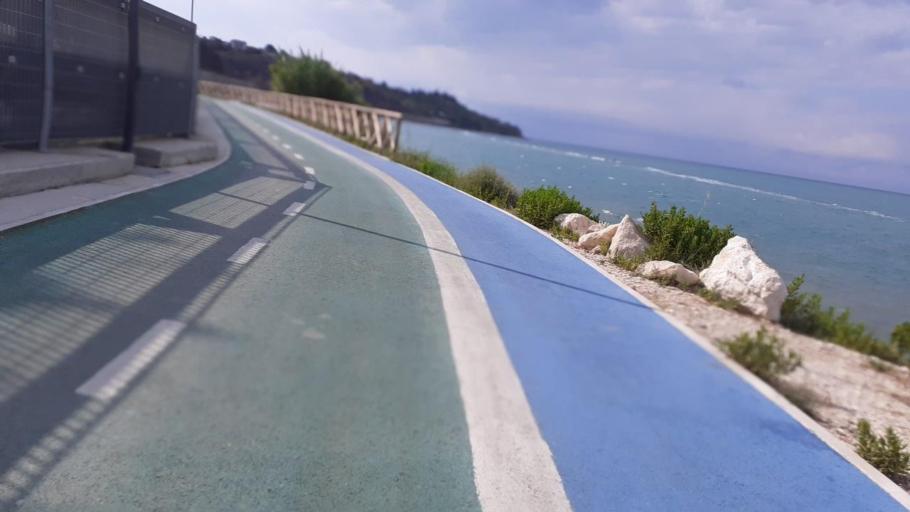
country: IT
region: Abruzzo
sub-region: Provincia di Chieti
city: Ortona
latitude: 42.3599
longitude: 14.4070
